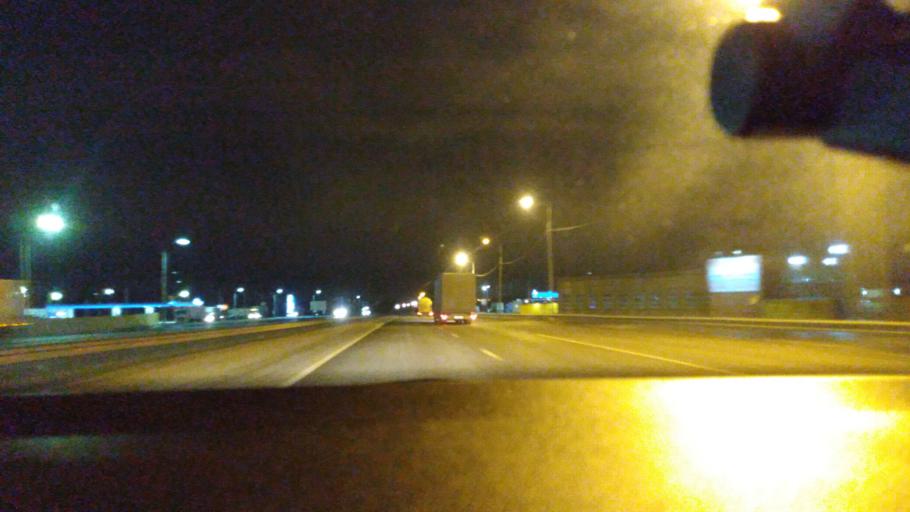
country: RU
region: Moskovskaya
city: Kolomna
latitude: 55.1225
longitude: 38.8117
